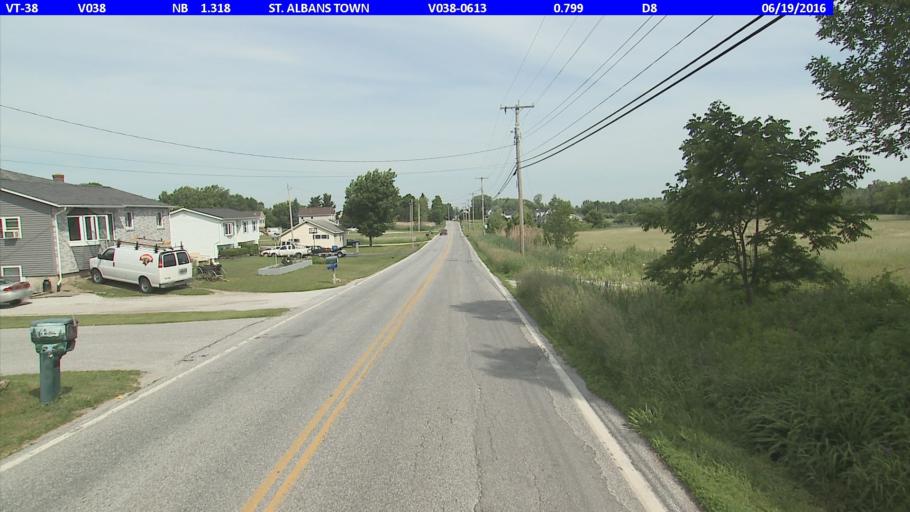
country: US
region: Vermont
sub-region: Franklin County
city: Saint Albans
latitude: 44.8341
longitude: -73.0968
